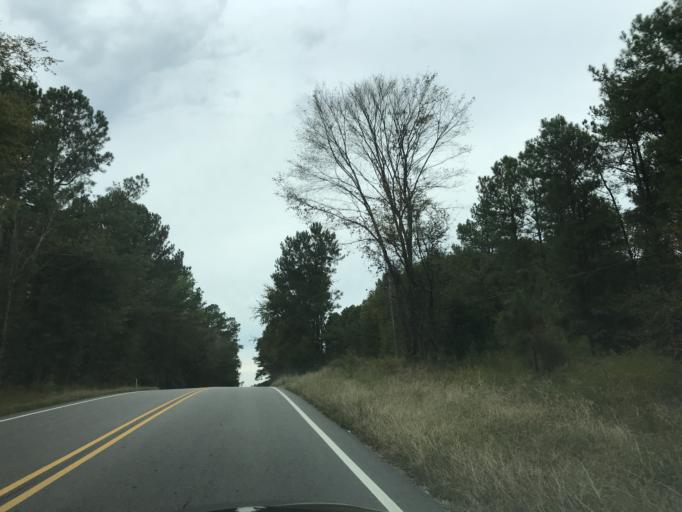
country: US
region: North Carolina
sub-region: Wake County
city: Knightdale
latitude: 35.8128
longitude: -78.4957
